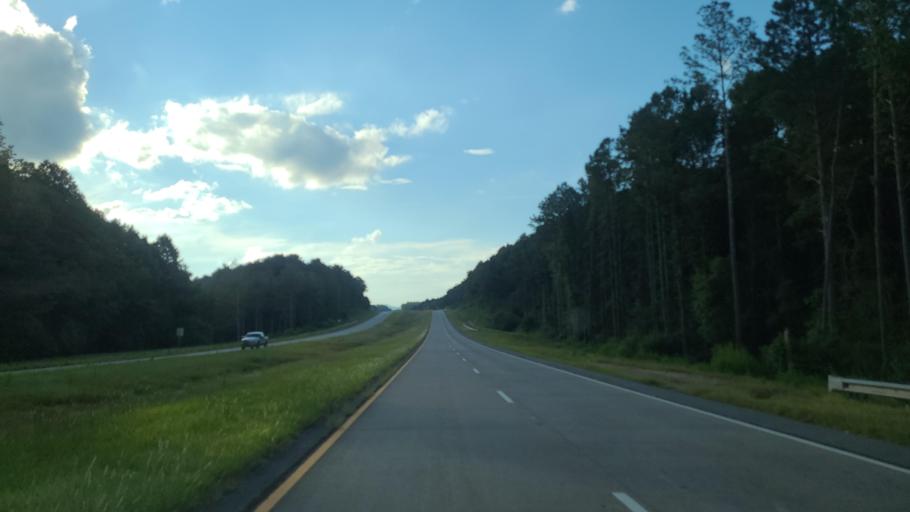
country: US
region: Georgia
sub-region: Pickens County
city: Nelson
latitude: 34.3776
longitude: -84.3859
